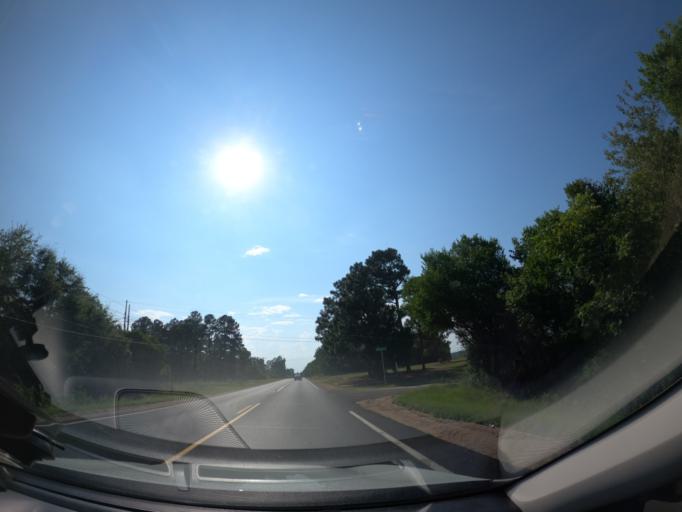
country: US
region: South Carolina
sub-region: Aiken County
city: New Ellenton
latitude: 33.3930
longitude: -81.7288
